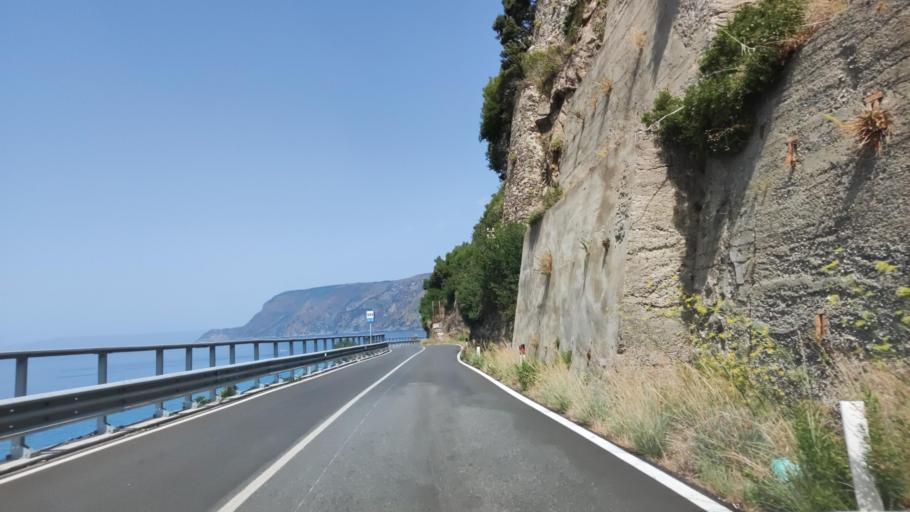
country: IT
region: Calabria
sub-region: Provincia di Reggio Calabria
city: Bagnara Calabra
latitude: 38.2751
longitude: 15.7858
